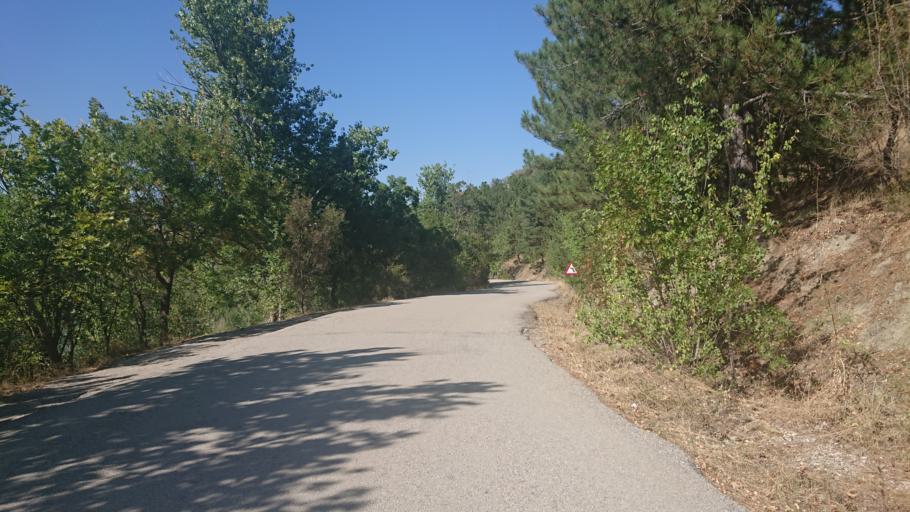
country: TR
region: Ankara
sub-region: Goelbasi
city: Golbasi
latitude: 39.8188
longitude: 32.8208
